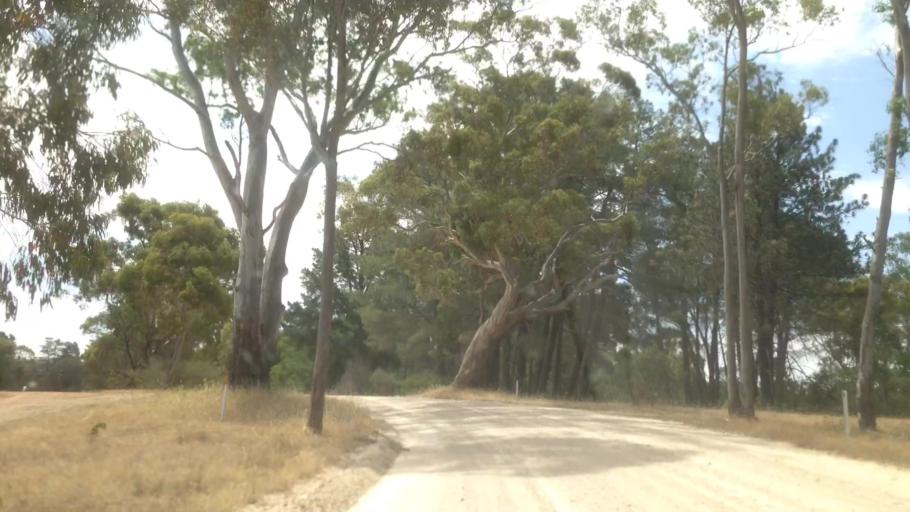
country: AU
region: South Australia
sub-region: Barossa
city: Williamstown
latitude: -34.7025
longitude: 138.9584
